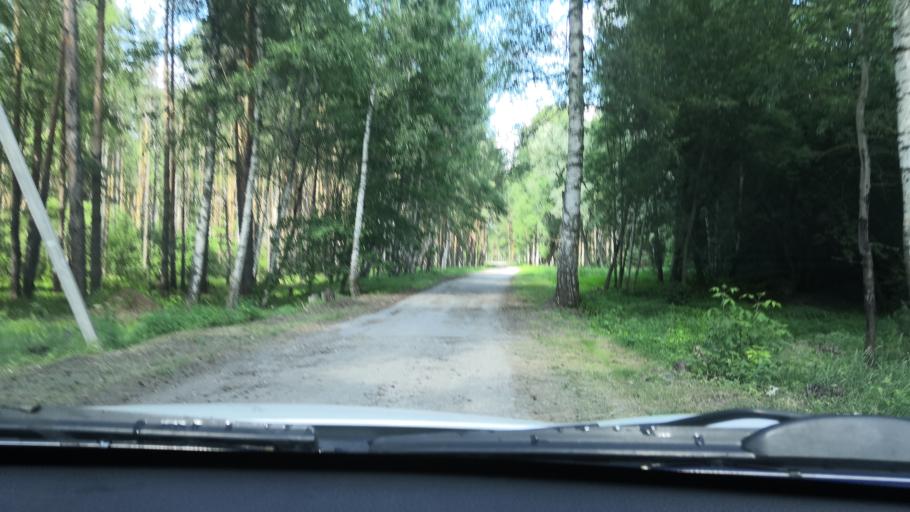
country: RU
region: Rjazan
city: Murmino
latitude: 54.5383
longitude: 40.1720
